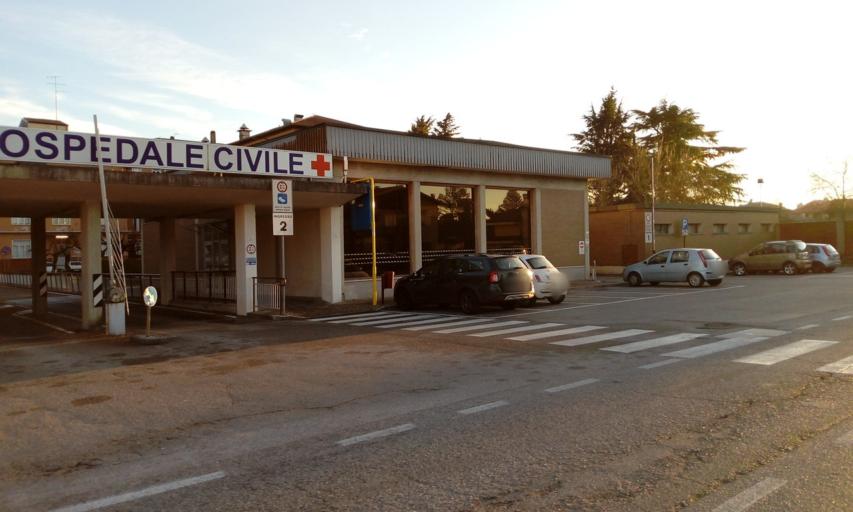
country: IT
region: Friuli Venezia Giulia
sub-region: Provincia di Udine
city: Cividale del Friuli
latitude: 46.0926
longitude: 13.4375
